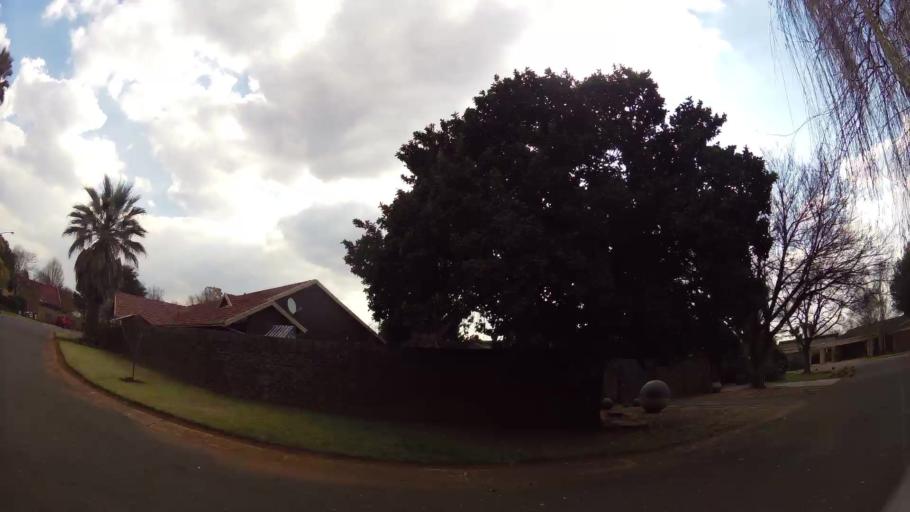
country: ZA
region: Mpumalanga
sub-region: Nkangala District Municipality
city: Delmas
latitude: -26.1451
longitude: 28.6850
